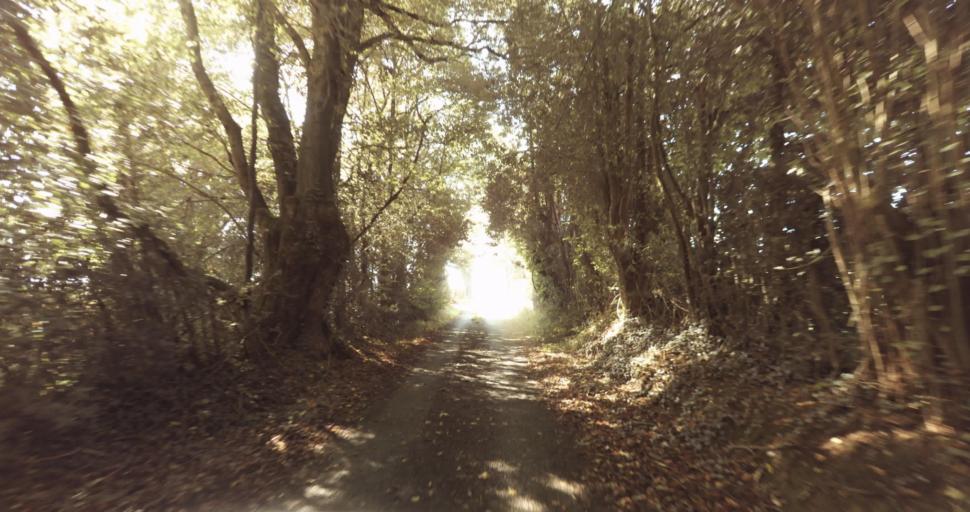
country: FR
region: Lower Normandy
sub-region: Departement du Calvados
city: Orbec
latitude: 48.9439
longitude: 0.3628
